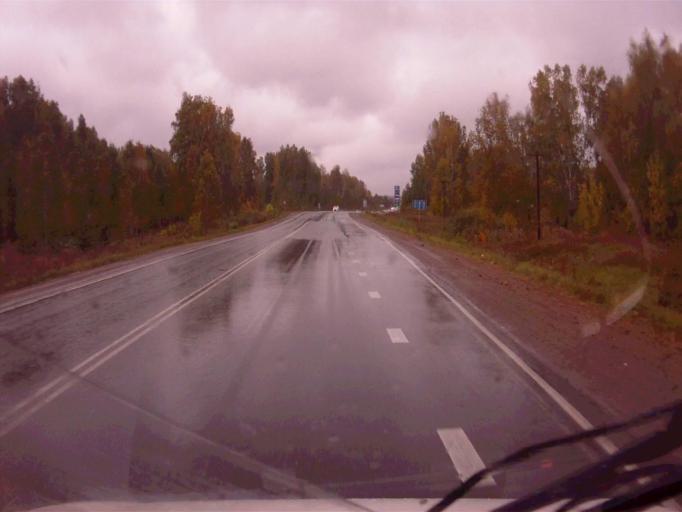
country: RU
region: Chelyabinsk
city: Argayash
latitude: 55.4703
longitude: 60.9033
